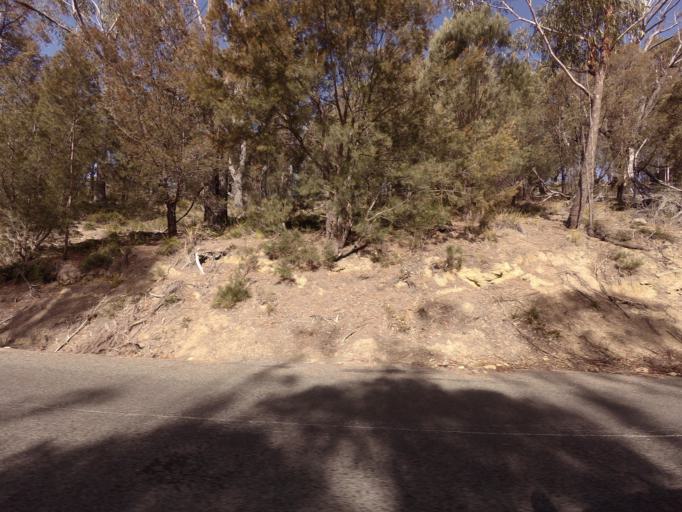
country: AU
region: Tasmania
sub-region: Break O'Day
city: St Helens
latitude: -41.6650
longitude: 148.2638
